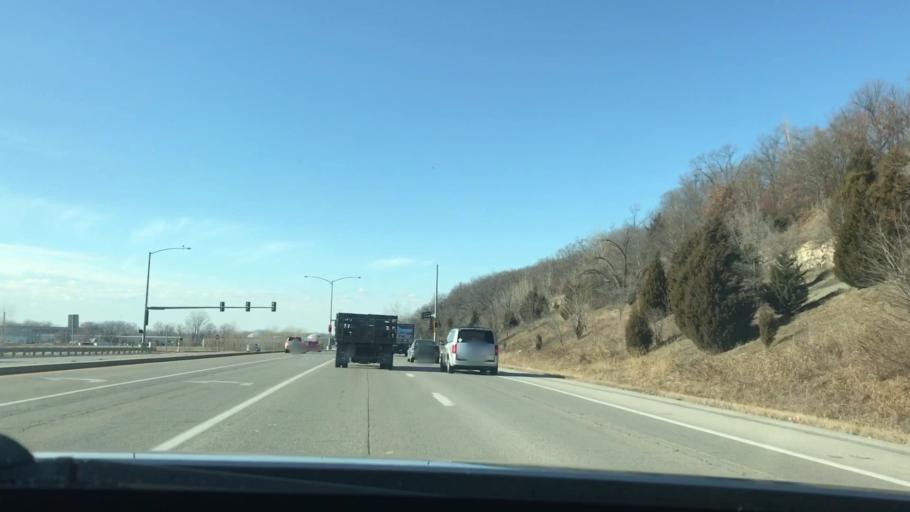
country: US
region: Missouri
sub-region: Platte County
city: Riverside
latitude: 39.1752
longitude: -94.6376
